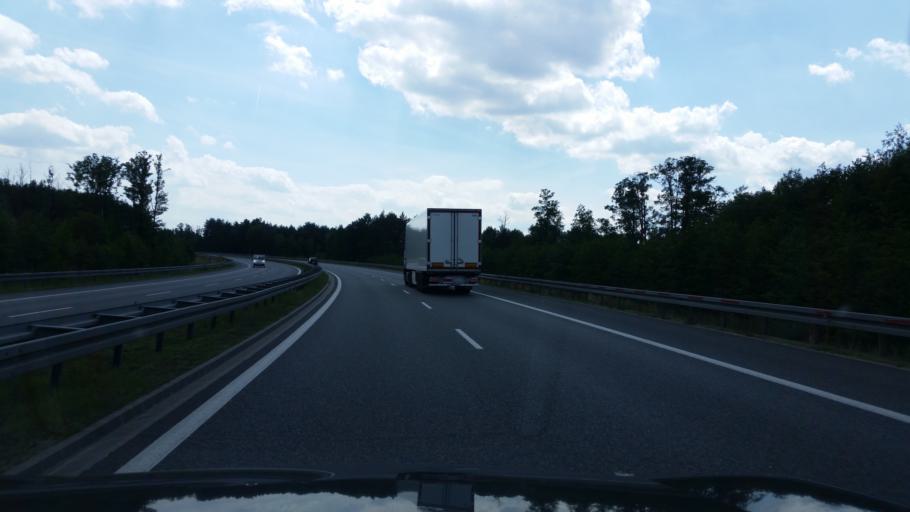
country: PL
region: Masovian Voivodeship
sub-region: Powiat wyszkowski
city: Wyszkow
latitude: 52.5690
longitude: 21.4701
